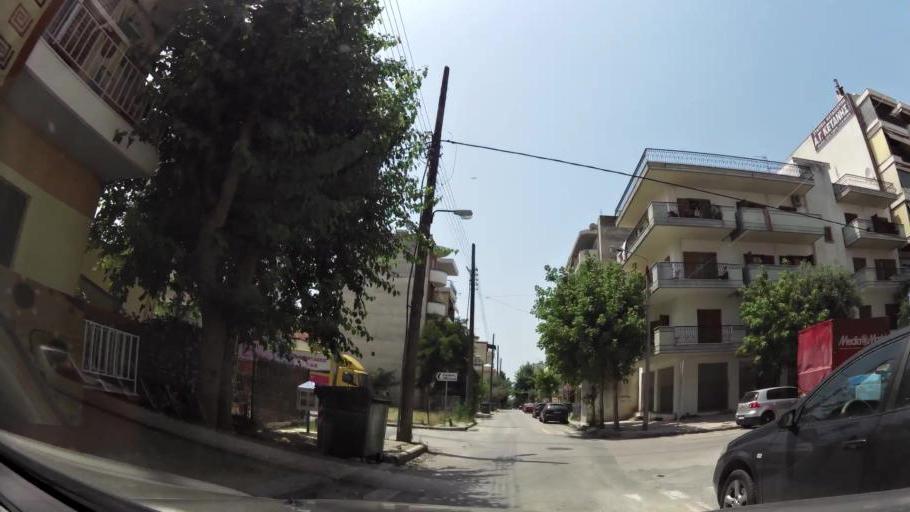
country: GR
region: Central Macedonia
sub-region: Nomos Thessalonikis
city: Menemeni
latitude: 40.6717
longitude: 22.8908
